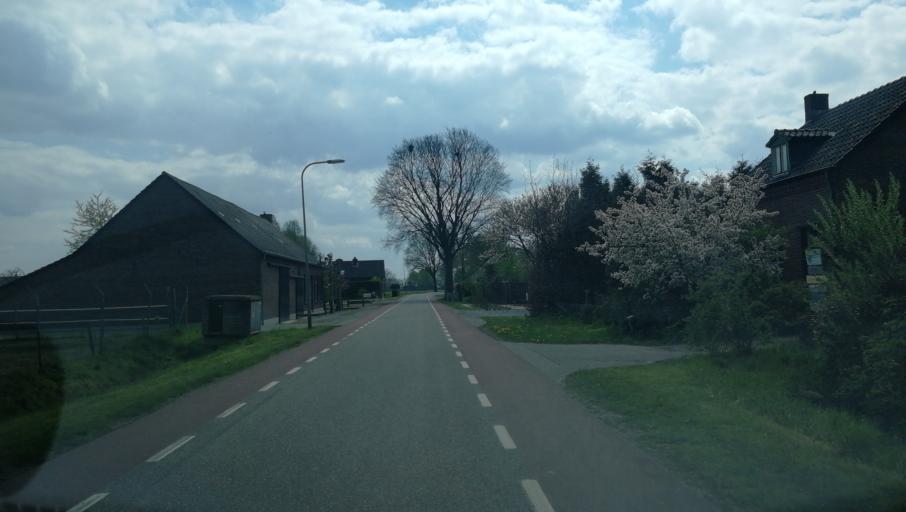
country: NL
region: Limburg
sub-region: Gemeente Peel en Maas
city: Maasbree
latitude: 51.4423
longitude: 6.0272
